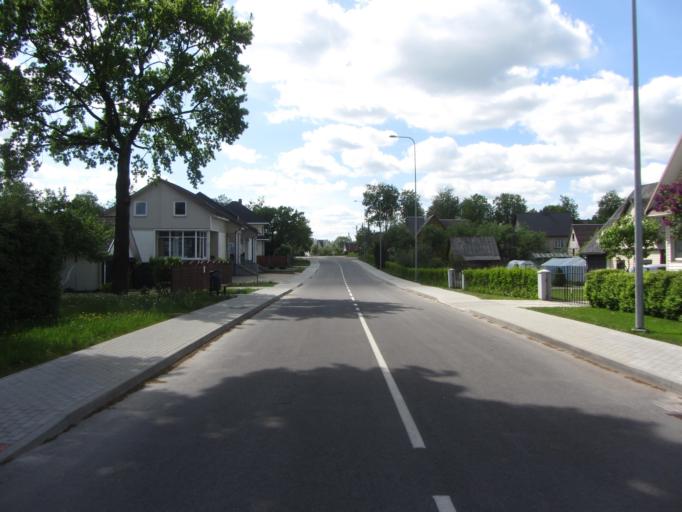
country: LT
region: Utenos apskritis
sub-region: Utena
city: Utena
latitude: 55.4998
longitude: 25.5925
